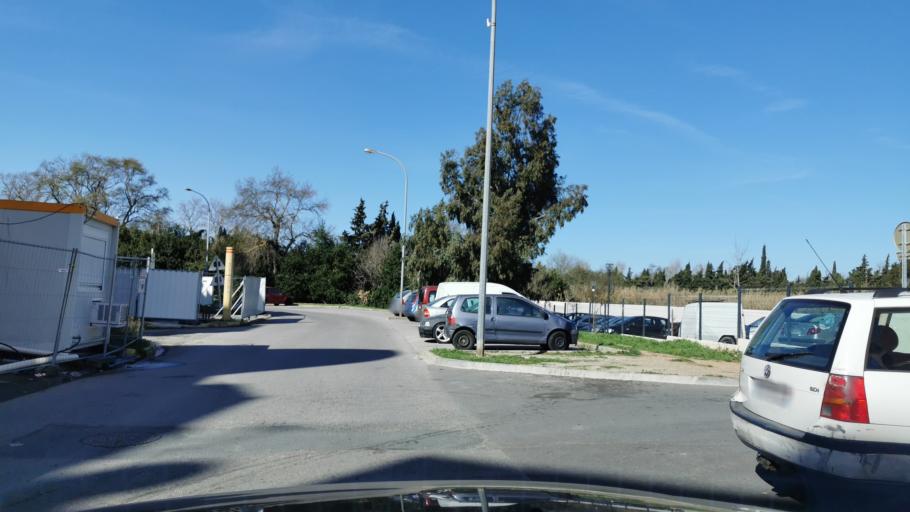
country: FR
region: Languedoc-Roussillon
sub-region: Departement de l'Aude
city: Narbonne
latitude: 43.1888
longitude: 2.9928
